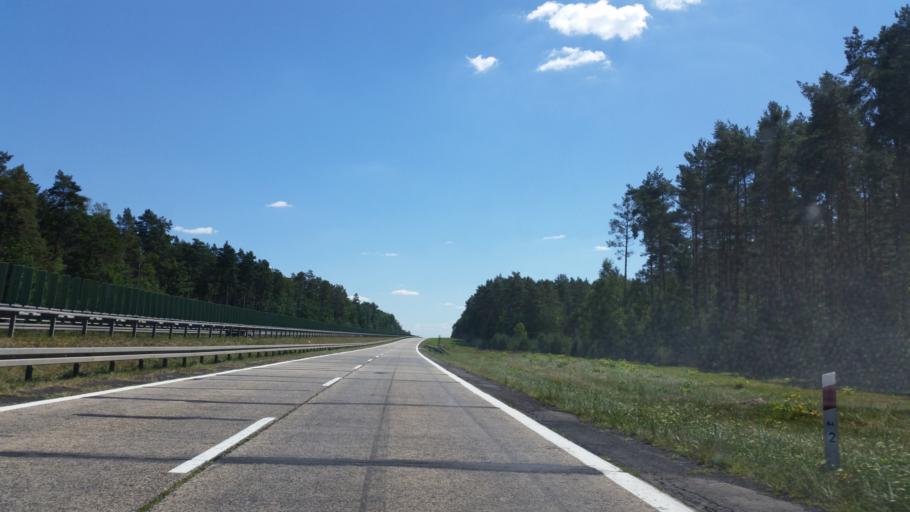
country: PL
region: Lower Silesian Voivodeship
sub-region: Powiat boleslawiecki
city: Boleslawiec
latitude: 51.3979
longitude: 15.5240
